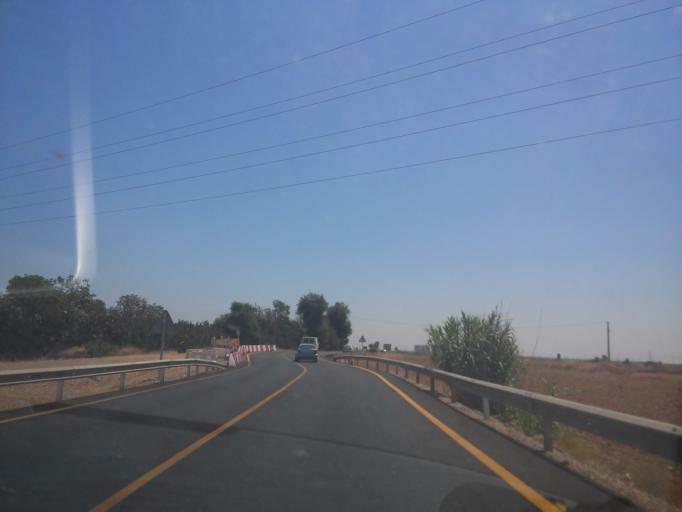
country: ES
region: Andalusia
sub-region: Provincia de Sevilla
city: La Rinconada
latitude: 37.4672
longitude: -5.9652
